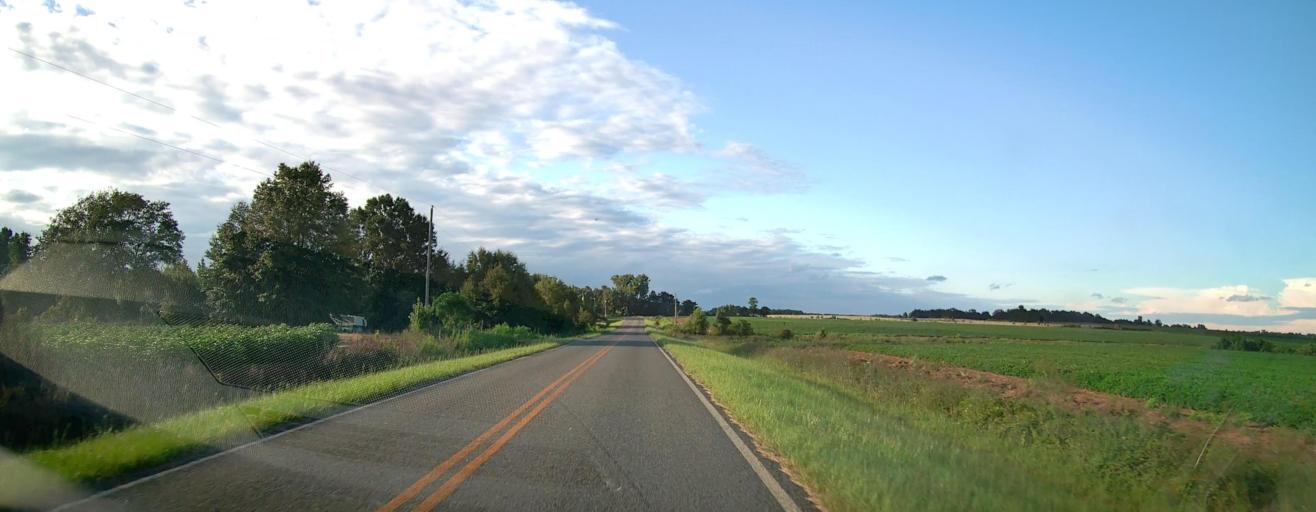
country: US
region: Georgia
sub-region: Pulaski County
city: Hawkinsville
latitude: 32.2784
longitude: -83.5386
